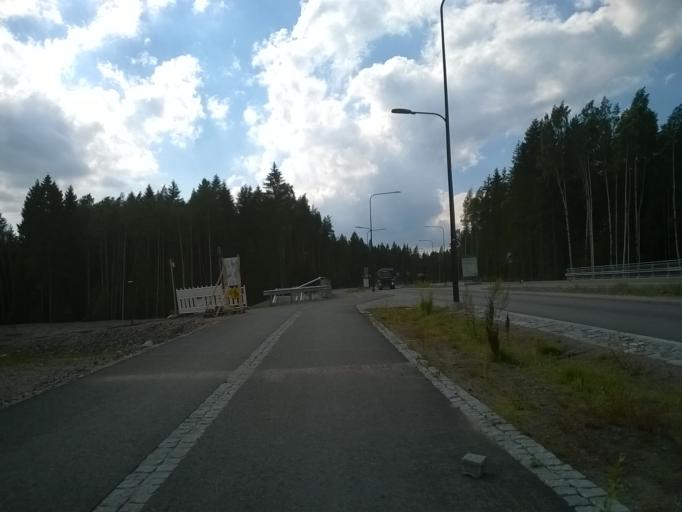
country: FI
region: Uusimaa
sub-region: Helsinki
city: Teekkarikylae
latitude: 60.2596
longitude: 24.8953
